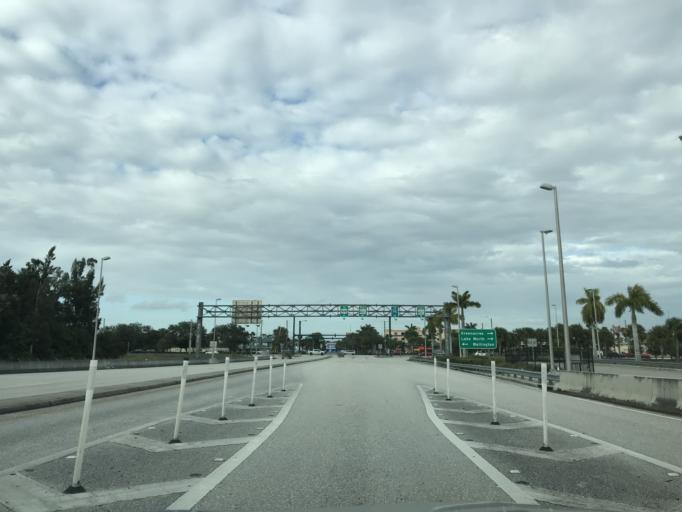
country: US
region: Florida
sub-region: Palm Beach County
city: Greenacres City
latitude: 26.6156
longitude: -80.1755
